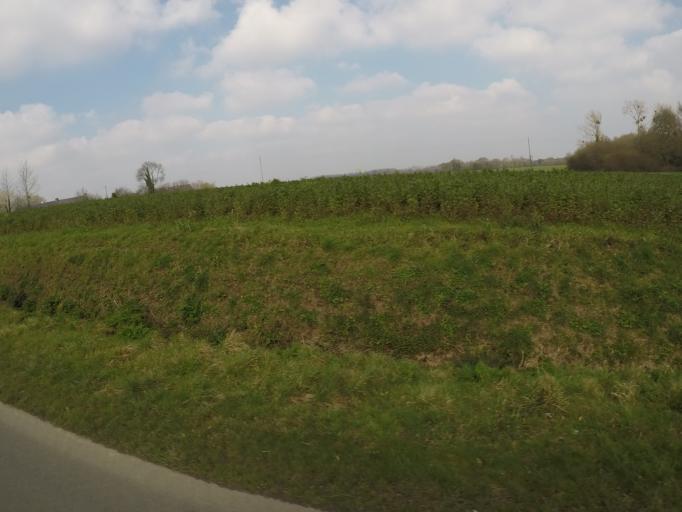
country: FR
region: Brittany
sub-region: Departement des Cotes-d'Armor
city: Pommerit-le-Vicomte
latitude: 48.6147
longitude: -3.0607
